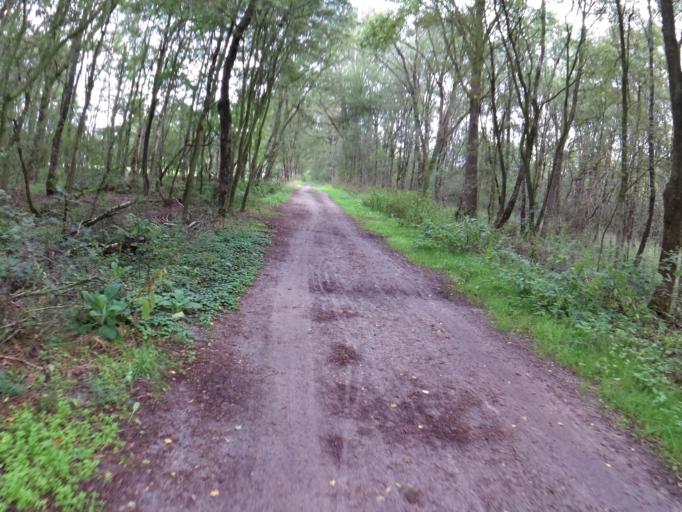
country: NL
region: Gelderland
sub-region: Berkelland
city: Eibergen
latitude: 52.0433
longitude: 6.6896
